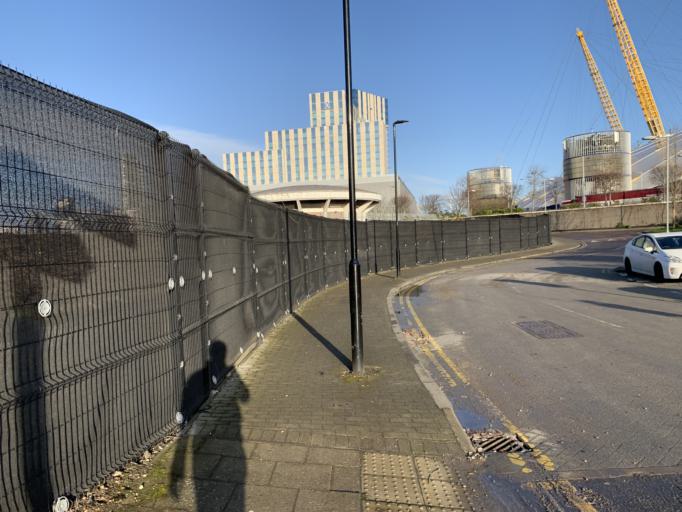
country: GB
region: England
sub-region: Greater London
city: Poplar
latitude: 51.5009
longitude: 0.0005
